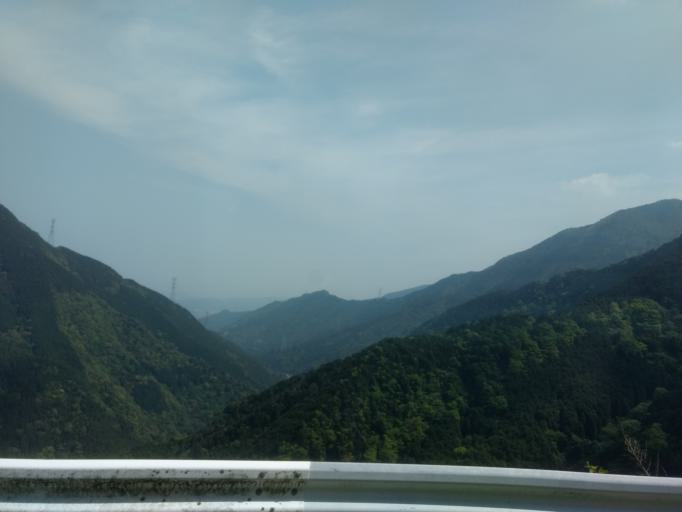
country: JP
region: Ehime
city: Niihama
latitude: 33.8753
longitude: 133.3002
